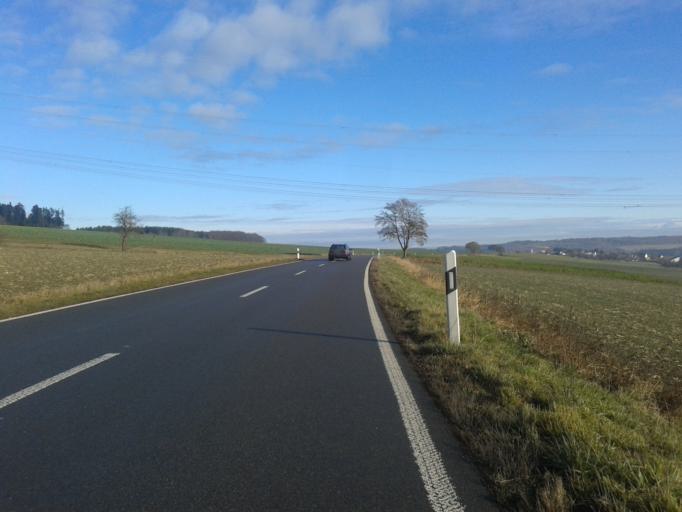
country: DE
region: Baden-Wuerttemberg
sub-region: Tuebingen Region
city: Blaubeuren
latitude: 48.3871
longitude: 9.8431
